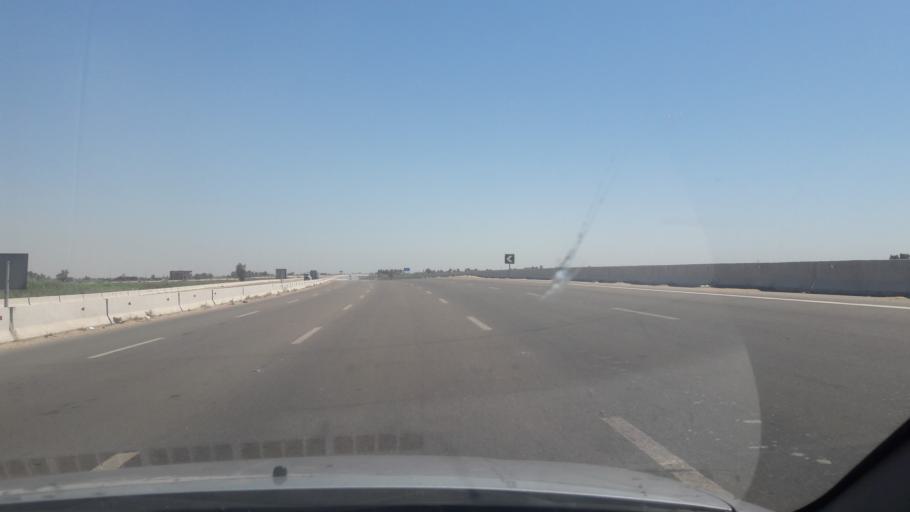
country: EG
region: Muhafazat Bur Sa`id
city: Port Said
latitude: 31.0888
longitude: 32.2329
